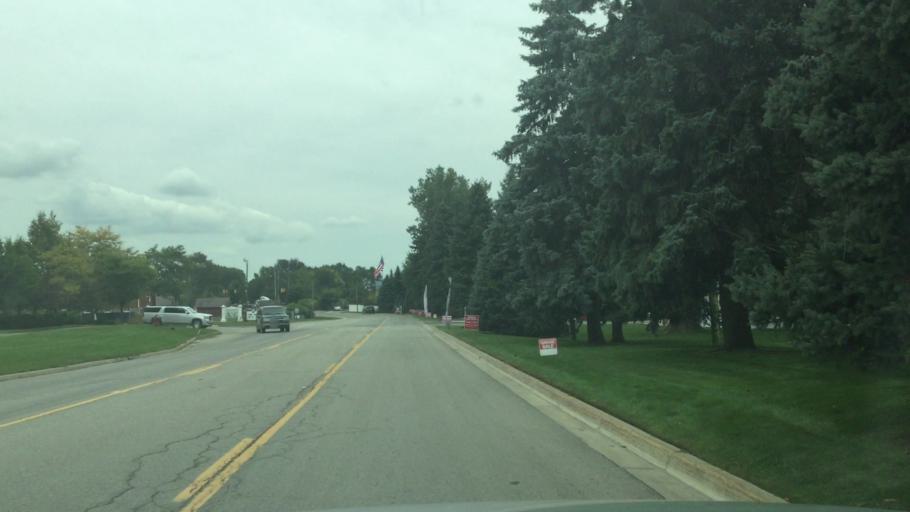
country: US
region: Michigan
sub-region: Oakland County
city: Waterford
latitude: 42.6598
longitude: -83.4690
